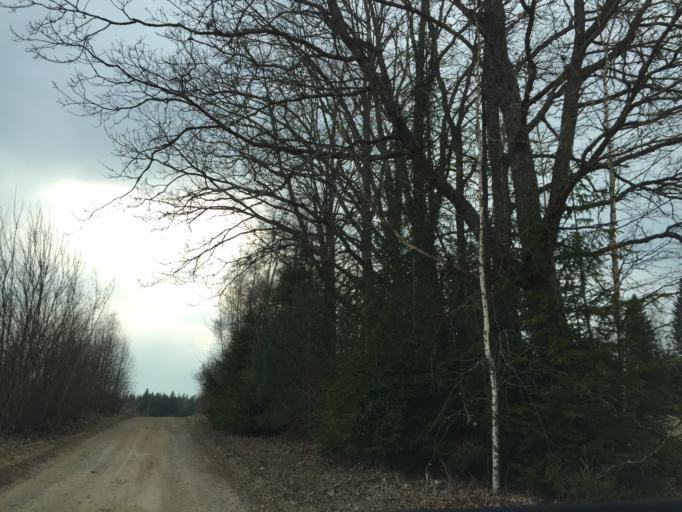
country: LV
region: Amatas Novads
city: Drabesi
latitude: 57.2107
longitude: 25.2514
